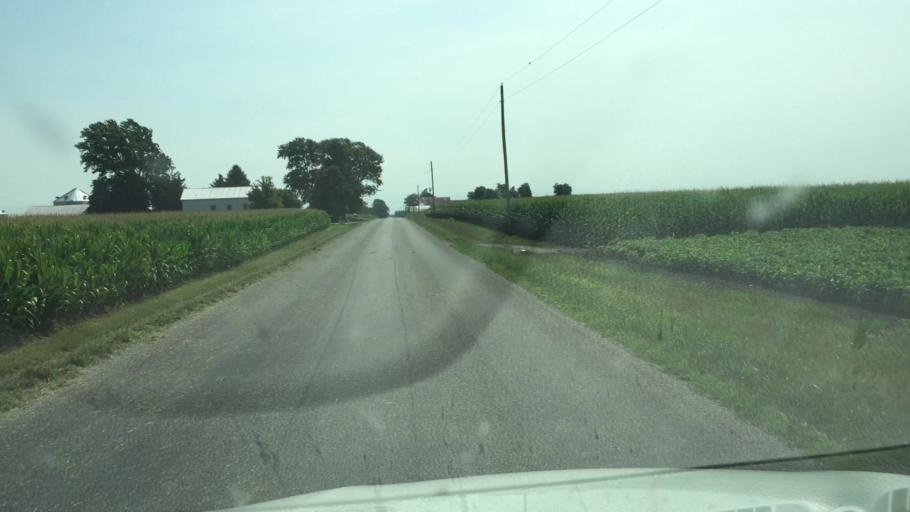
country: US
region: Illinois
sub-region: Hancock County
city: Nauvoo
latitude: 40.5073
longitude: -91.3161
